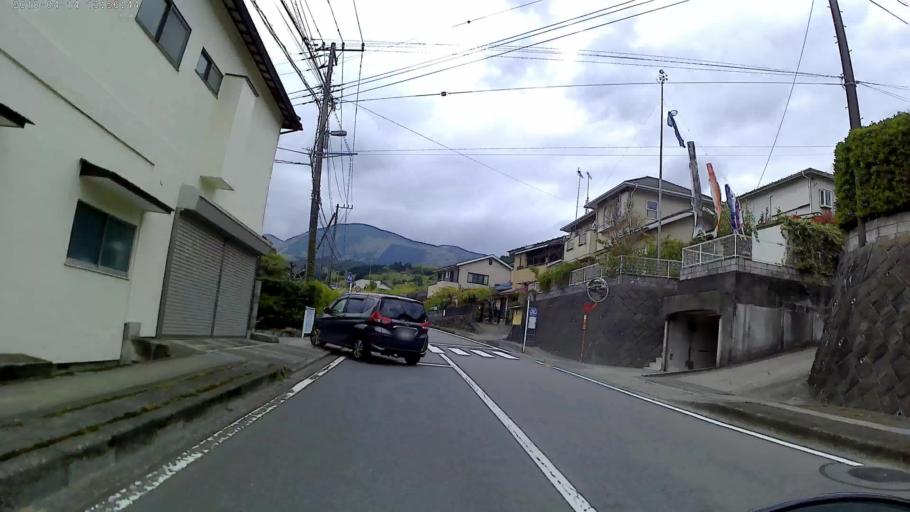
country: JP
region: Kanagawa
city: Odawara
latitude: 35.3314
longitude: 139.0793
